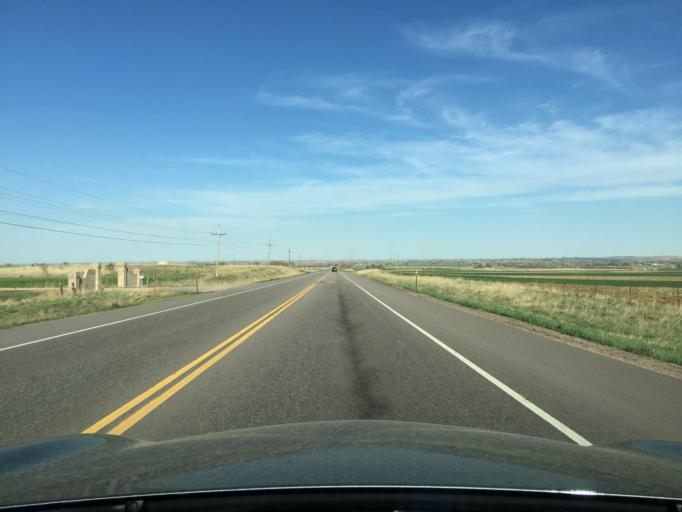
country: US
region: Colorado
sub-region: Boulder County
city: Niwot
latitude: 40.0874
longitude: -105.1282
